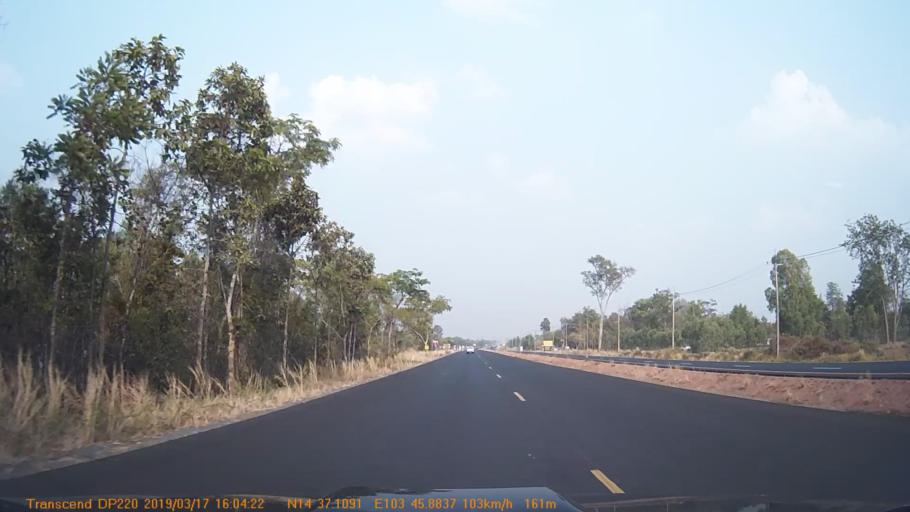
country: TH
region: Surin
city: Sangkha
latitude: 14.6185
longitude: 103.7650
